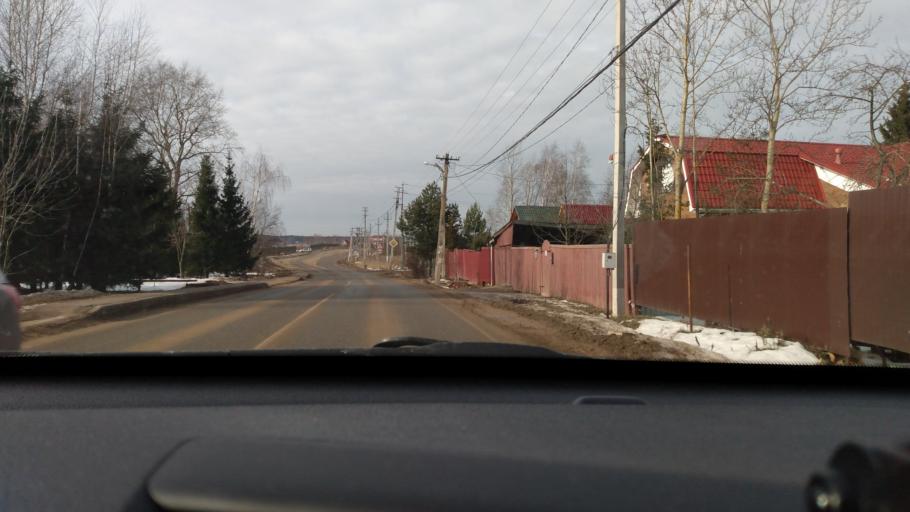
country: RU
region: Moskovskaya
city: Nakhabino
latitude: 55.8920
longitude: 37.1696
